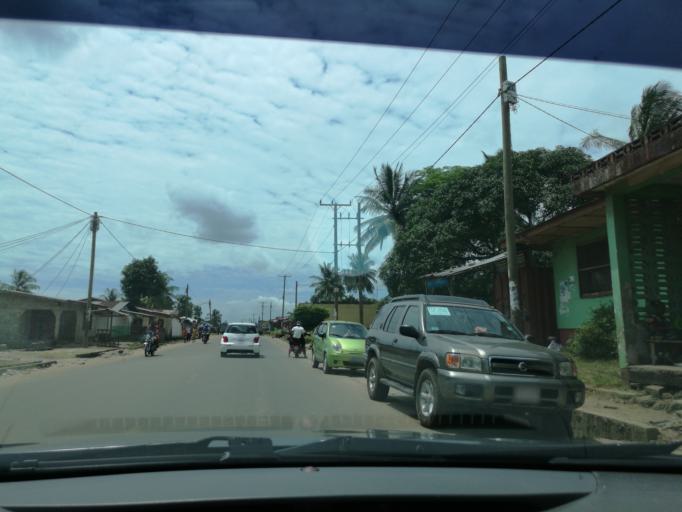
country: LR
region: Montserrado
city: Monrovia
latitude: 6.2919
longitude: -10.6807
